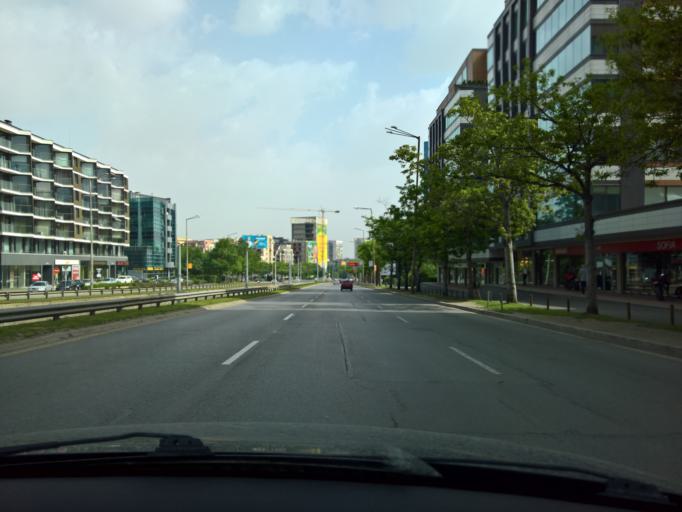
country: BG
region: Sofia-Capital
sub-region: Stolichna Obshtina
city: Sofia
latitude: 42.6628
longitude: 23.2865
